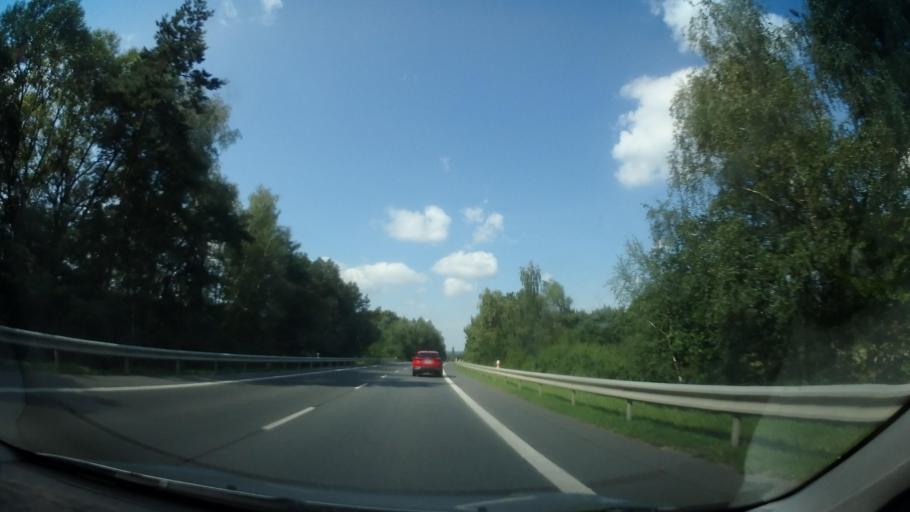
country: CZ
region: Central Bohemia
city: Kostelec nad Cernymi Lesy
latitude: 49.9875
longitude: 14.8400
